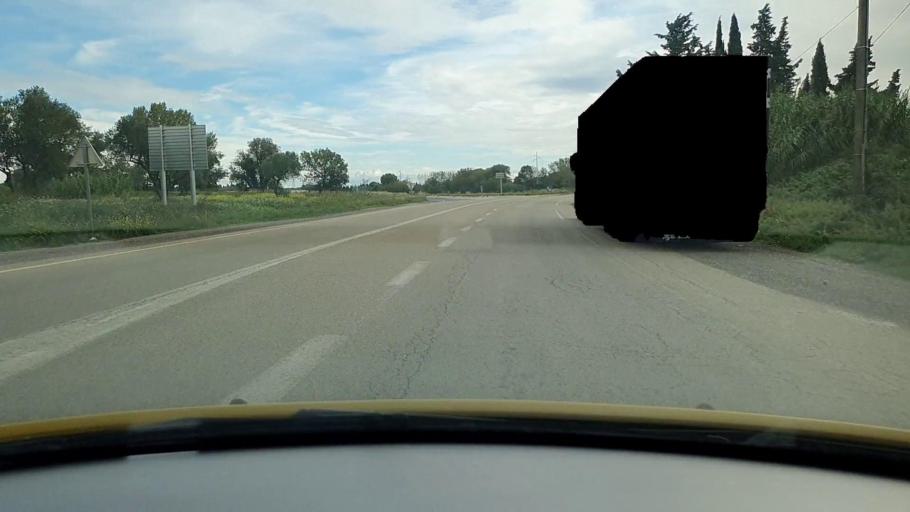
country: FR
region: Languedoc-Roussillon
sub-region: Departement du Gard
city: Bellegarde
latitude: 43.7463
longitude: 4.5212
